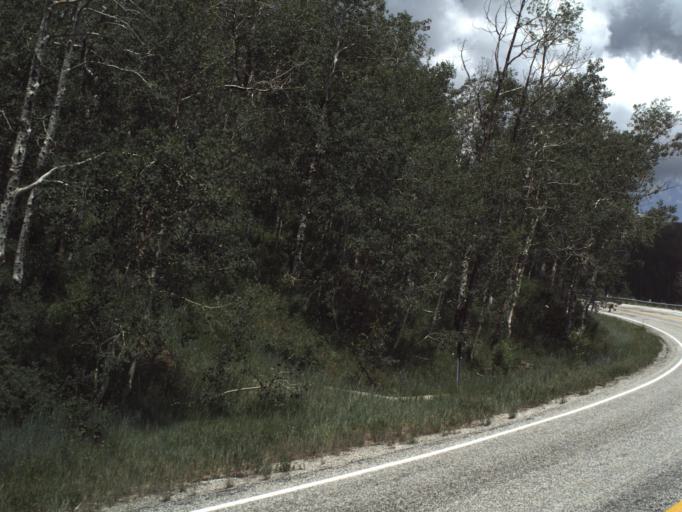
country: US
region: Utah
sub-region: Weber County
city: Wolf Creek
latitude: 41.4044
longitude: -111.5475
